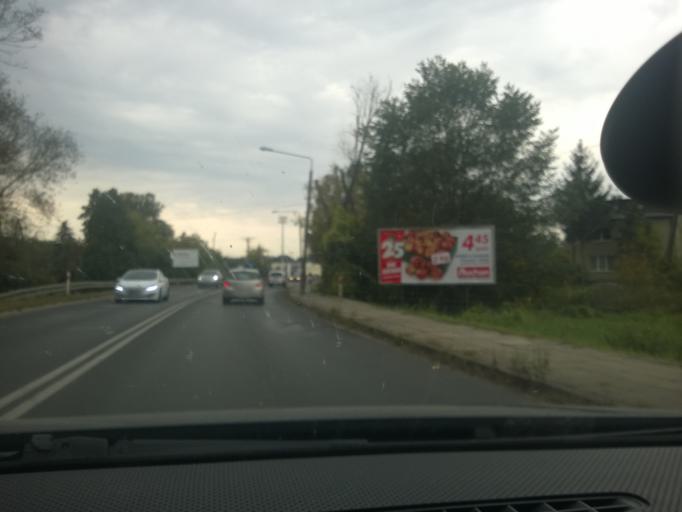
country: PL
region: Masovian Voivodeship
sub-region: Powiat pruszkowski
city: Pruszkow
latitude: 52.1709
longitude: 20.8202
